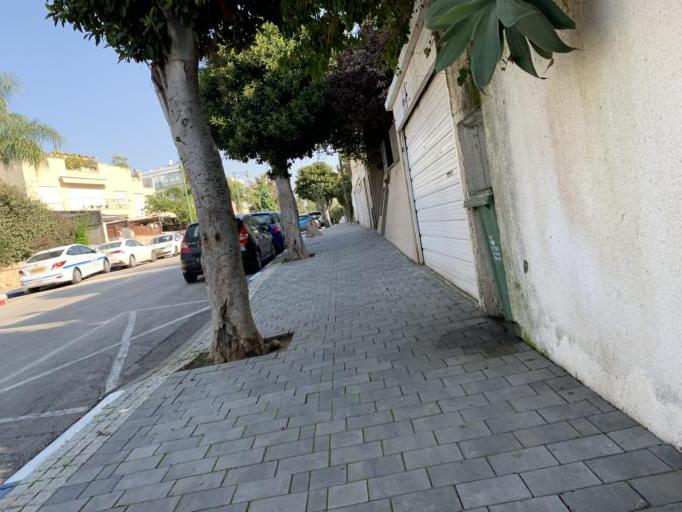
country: IL
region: Tel Aviv
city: Ramat Gan
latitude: 32.0921
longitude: 34.8131
